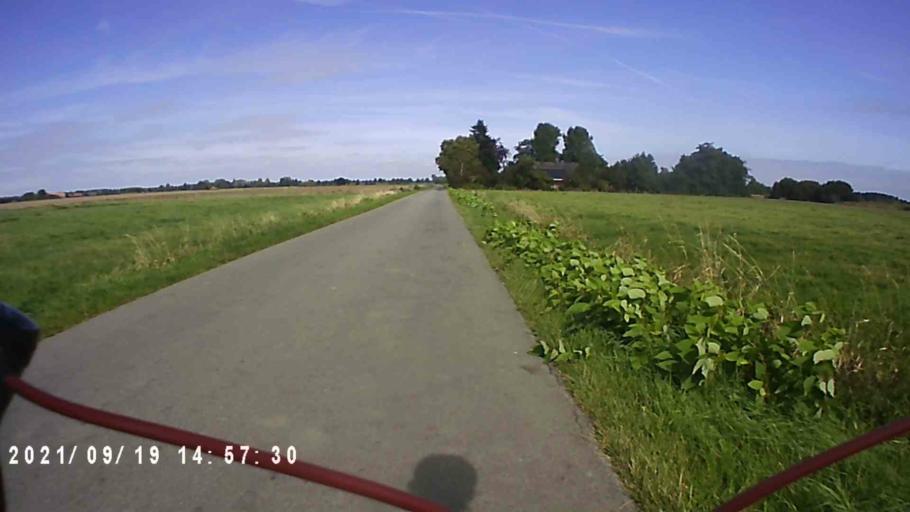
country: DE
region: Lower Saxony
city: Bunde
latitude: 53.1479
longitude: 7.2082
